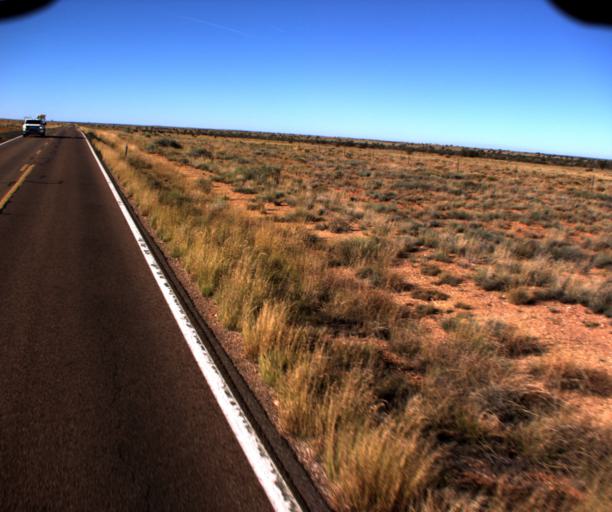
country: US
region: Arizona
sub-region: Navajo County
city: Holbrook
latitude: 34.7700
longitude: -110.2426
